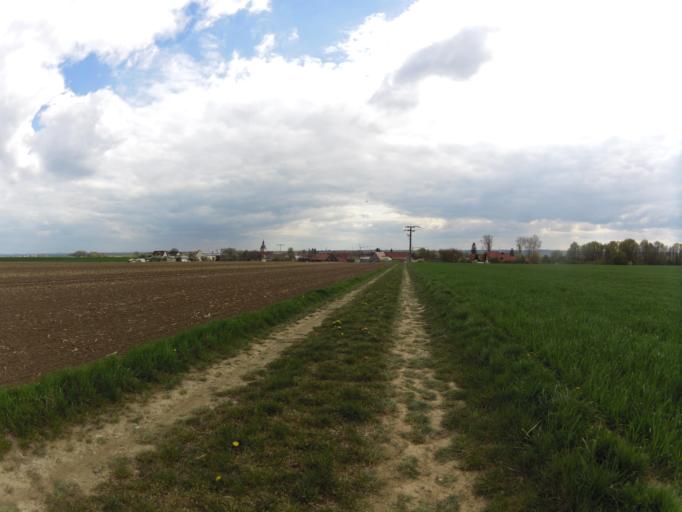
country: DE
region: Bavaria
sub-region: Regierungsbezirk Unterfranken
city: Giebelstadt
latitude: 49.6363
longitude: 9.9435
